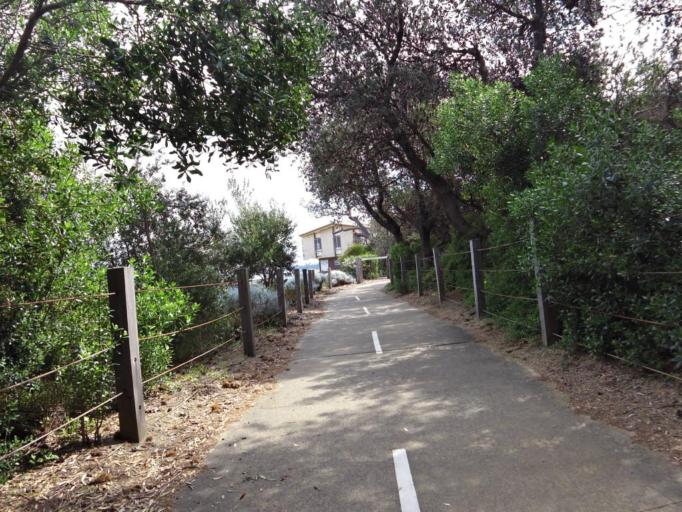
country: AU
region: Victoria
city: Beaumaris
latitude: -37.9899
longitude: 145.0285
